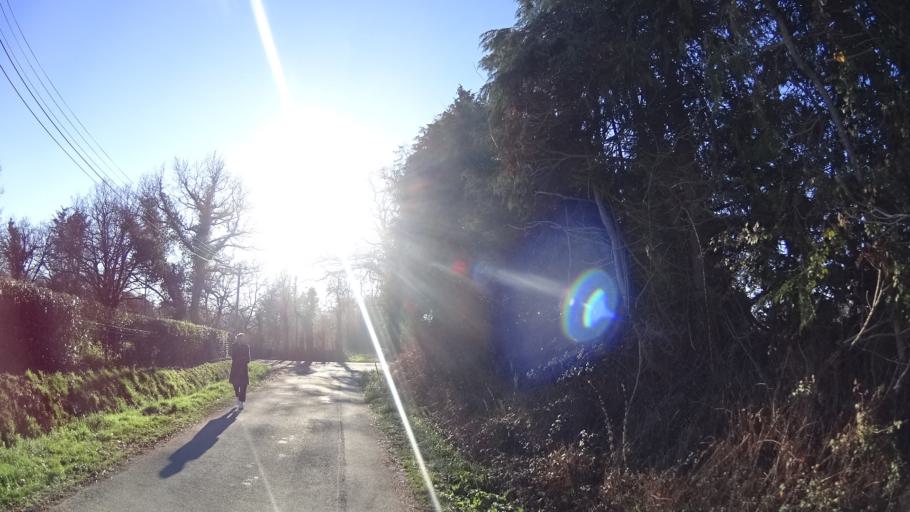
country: FR
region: Brittany
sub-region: Departement du Morbihan
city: Allaire
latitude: 47.6307
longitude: -2.1570
